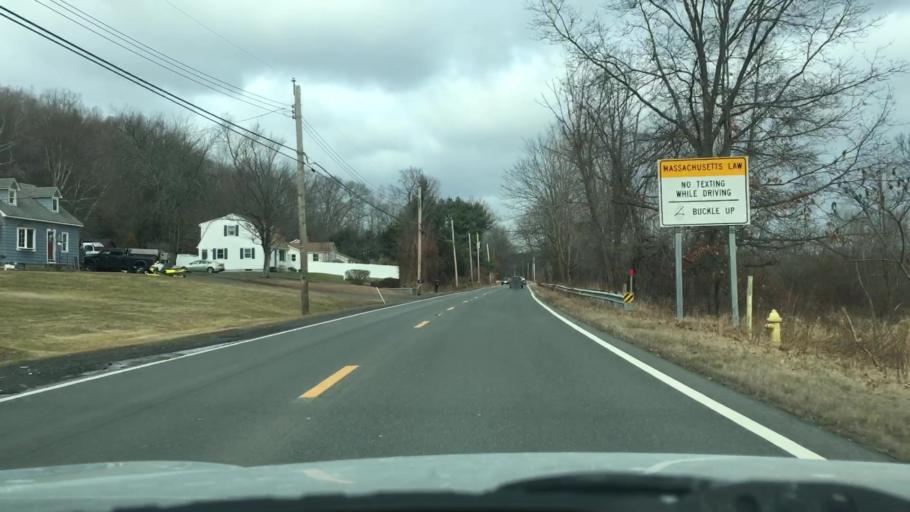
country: US
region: Connecticut
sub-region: Hartford County
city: North Granby
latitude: 42.0055
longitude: -72.7954
